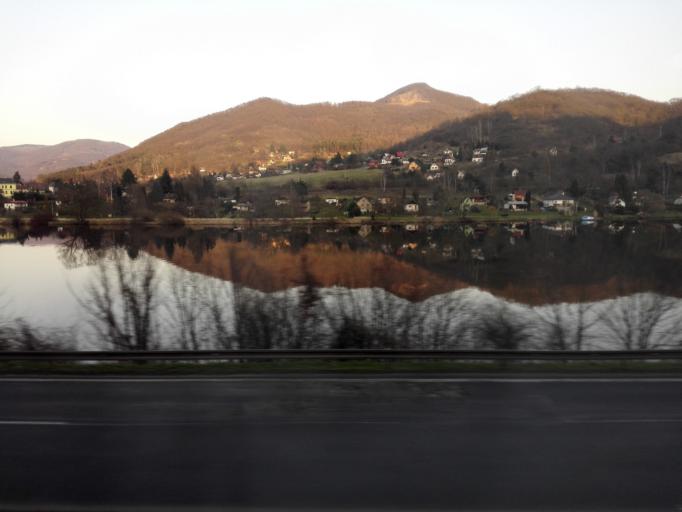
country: CZ
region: Ustecky
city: Trmice
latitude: 50.5876
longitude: 14.0296
